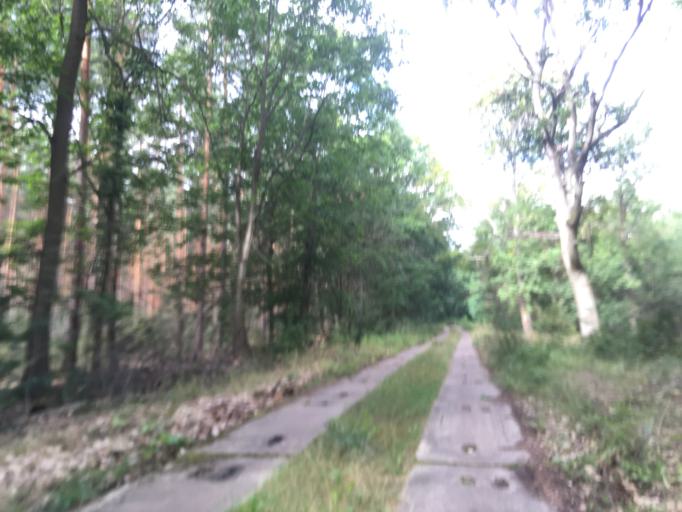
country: DE
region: Berlin
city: Schmockwitz
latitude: 52.3355
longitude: 13.6864
